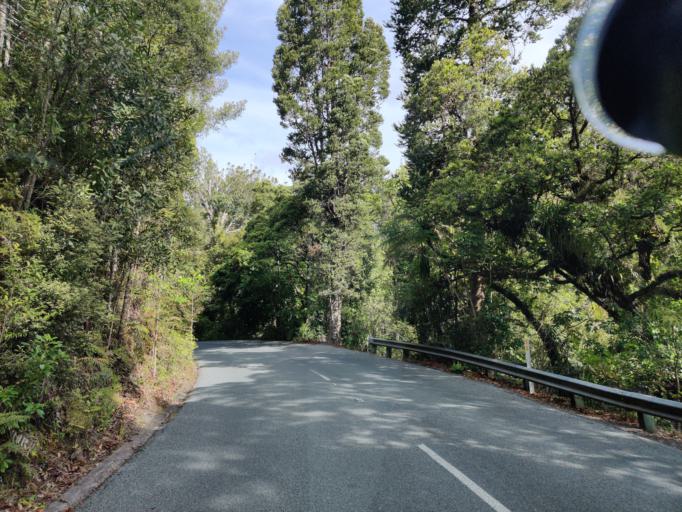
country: NZ
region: Northland
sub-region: Kaipara District
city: Dargaville
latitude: -35.6503
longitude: 173.5655
